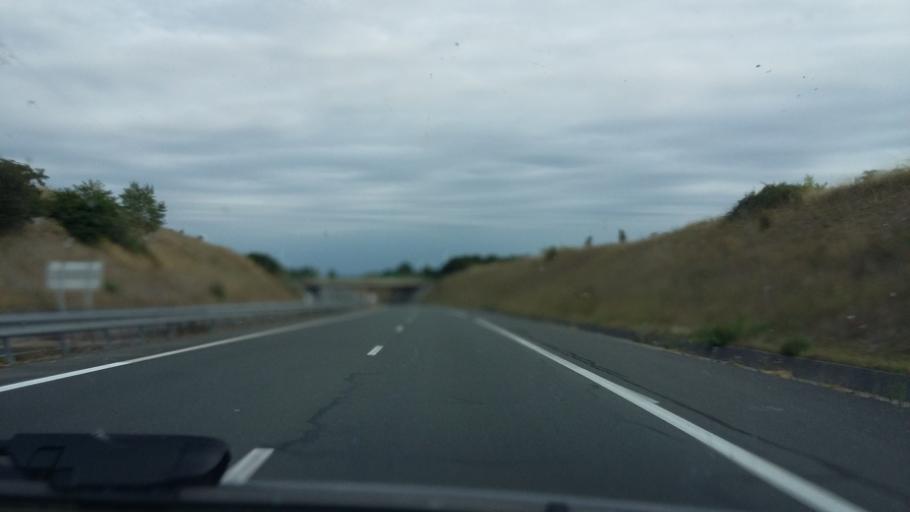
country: FR
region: Poitou-Charentes
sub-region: Departement de la Charente
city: Saint-Yrieix-sur-Charente
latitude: 45.6901
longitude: 0.1036
